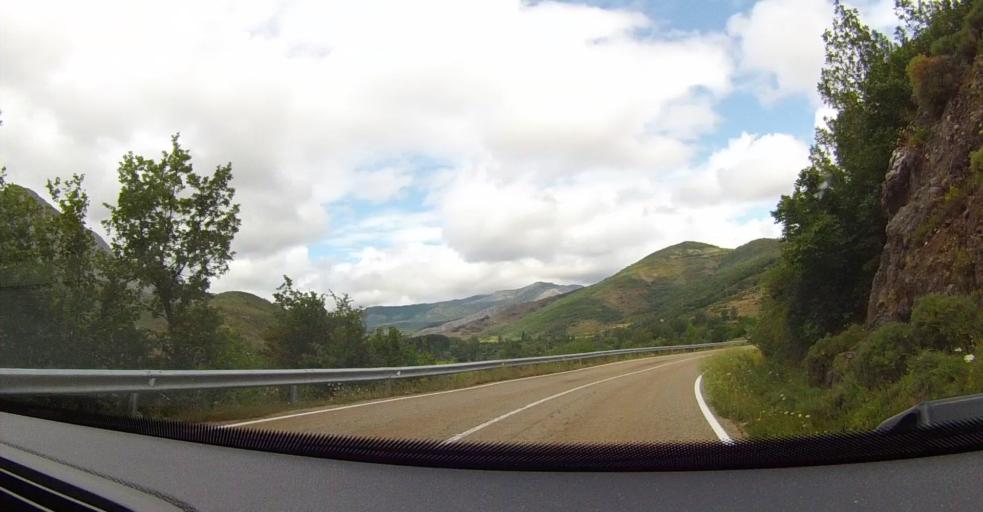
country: ES
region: Castille and Leon
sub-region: Provincia de Leon
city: Puebla de Lillo
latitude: 42.9747
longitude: -5.2595
